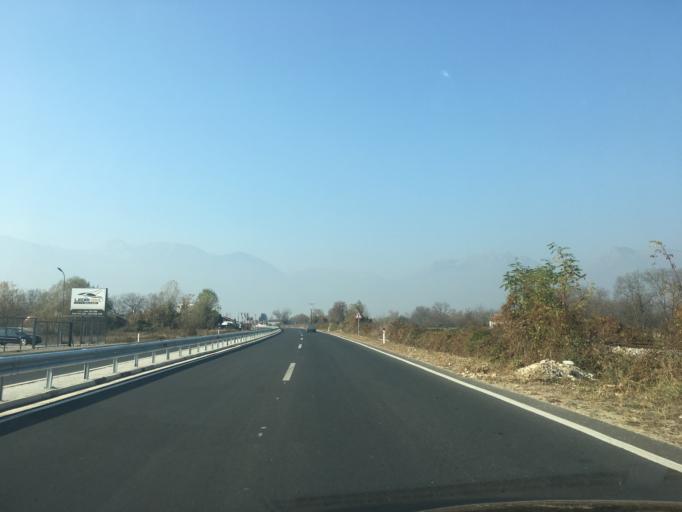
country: XK
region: Pec
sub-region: Komuna e Pejes
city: Dubova (Driloni)
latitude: 42.6596
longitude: 20.3668
